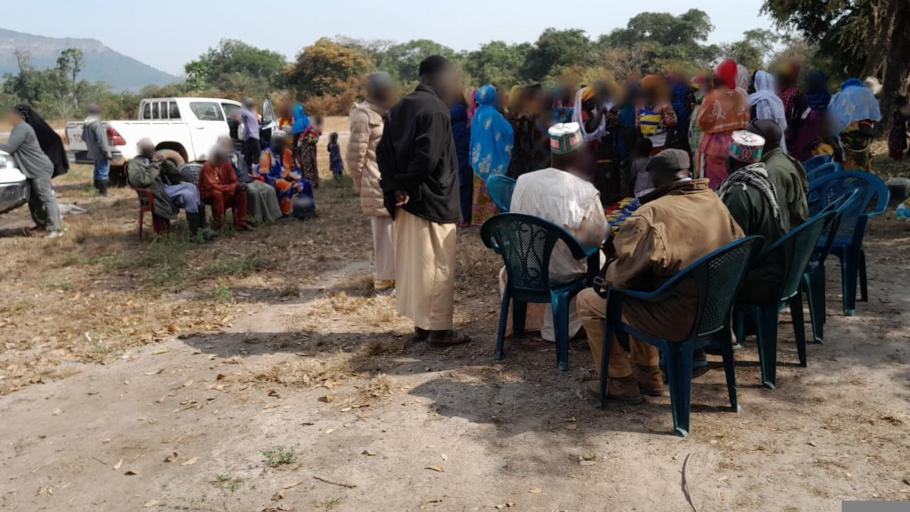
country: GN
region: Mamou
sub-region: Pita
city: Pita
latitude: 11.0157
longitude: -12.2279
